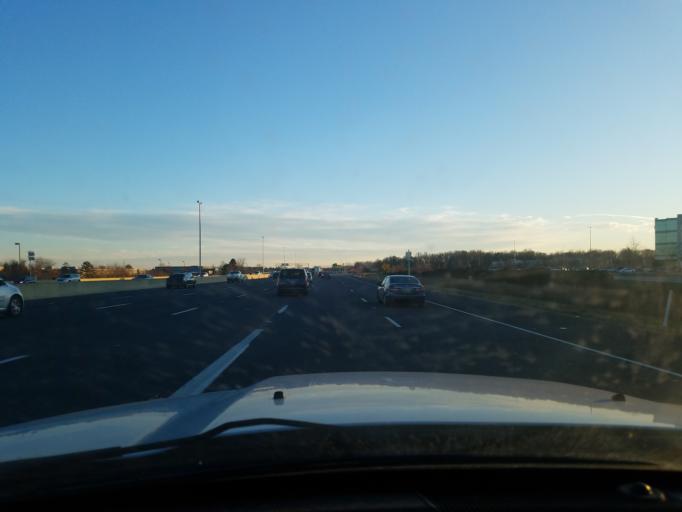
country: US
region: Indiana
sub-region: Marion County
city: Speedway
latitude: 39.8758
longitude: -86.2691
